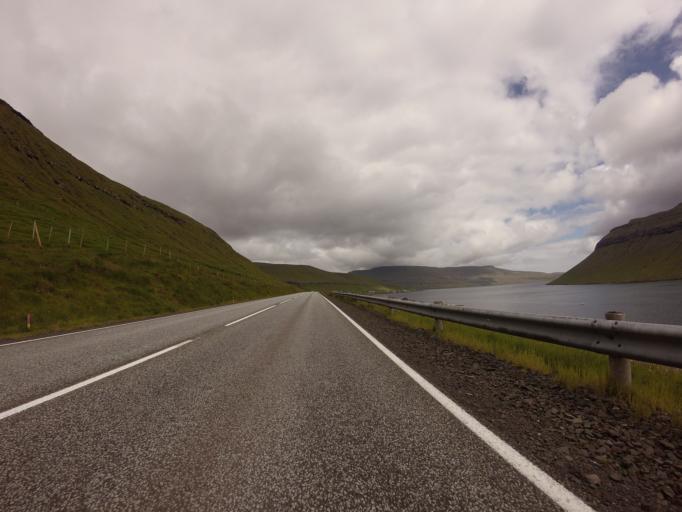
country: FO
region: Streymoy
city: Kollafjordhur
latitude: 62.1059
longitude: -6.9249
